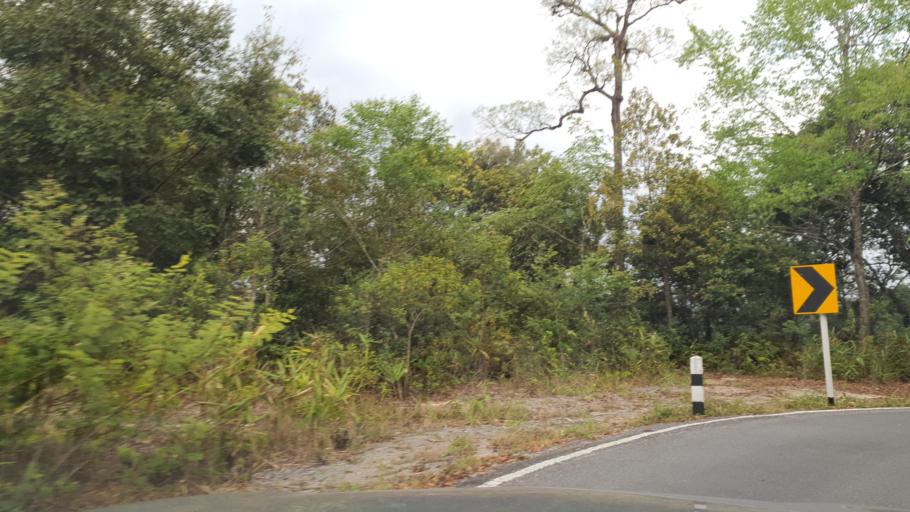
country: TH
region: Lampang
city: Mueang Pan
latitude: 18.9364
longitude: 99.3886
